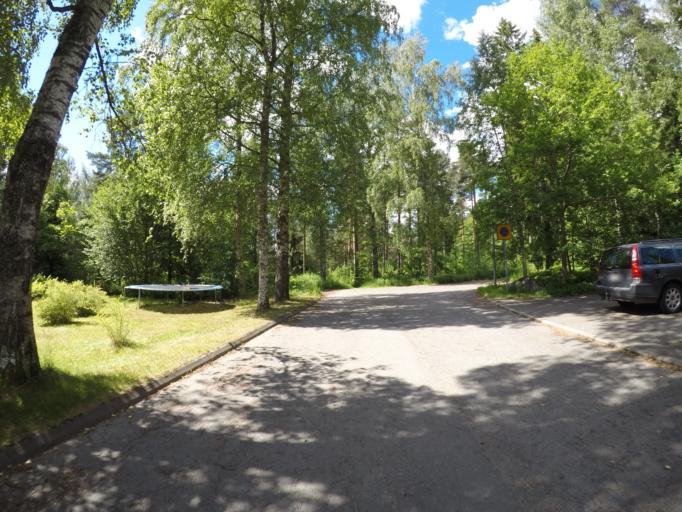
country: FI
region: Haeme
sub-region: Haemeenlinna
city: Haemeenlinna
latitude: 61.0128
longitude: 24.4343
